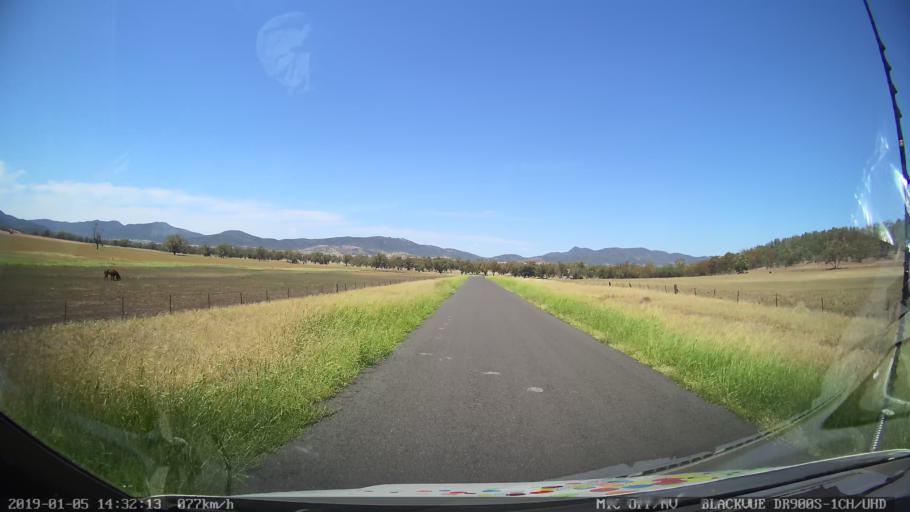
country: AU
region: New South Wales
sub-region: Tamworth Municipality
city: Phillip
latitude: -31.2216
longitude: 150.6154
